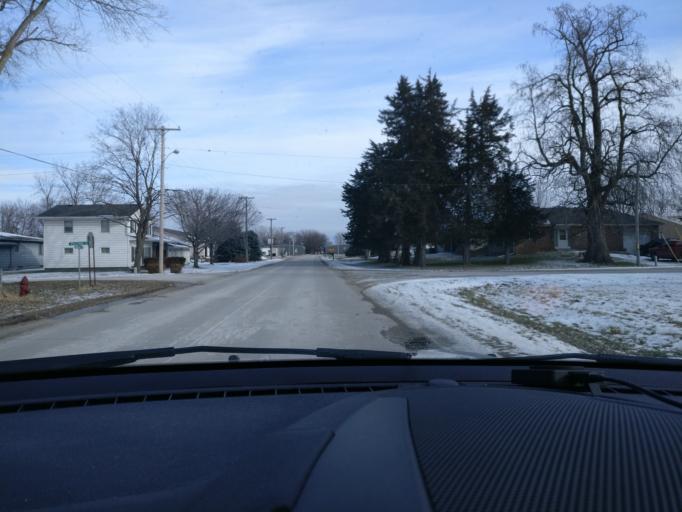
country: US
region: Nebraska
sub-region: Dodge County
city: Fremont
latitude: 41.4142
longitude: -96.5038
